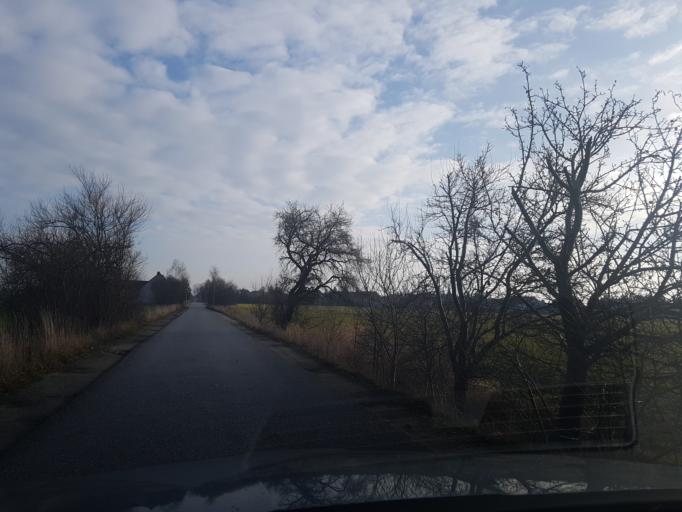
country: DE
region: Brandenburg
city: Ruckersdorf
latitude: 51.5364
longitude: 13.6159
